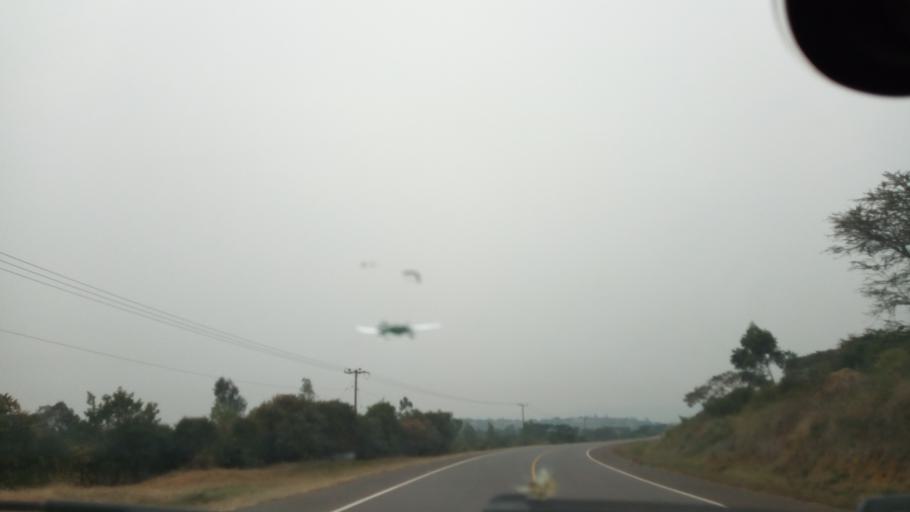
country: UG
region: Western Region
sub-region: Mbarara District
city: Mbarara
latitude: -0.7133
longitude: 30.7197
